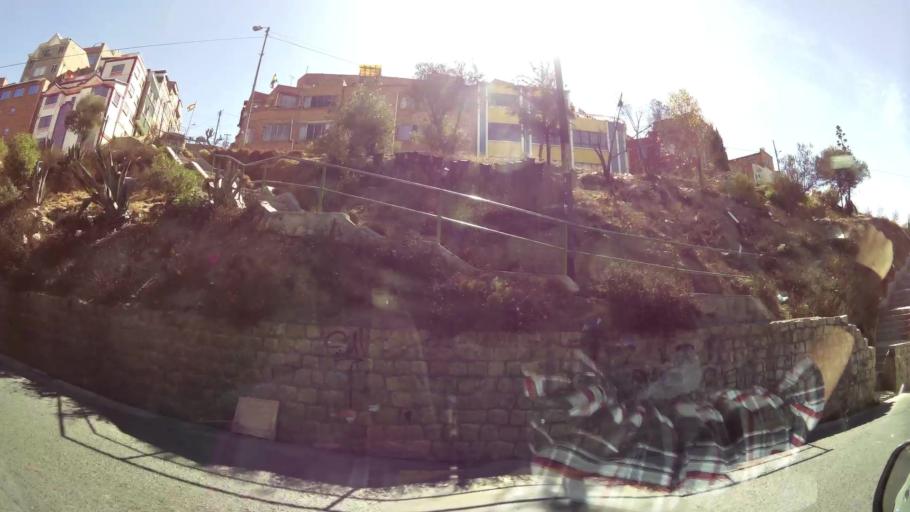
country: BO
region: La Paz
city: La Paz
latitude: -16.4911
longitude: -68.1471
